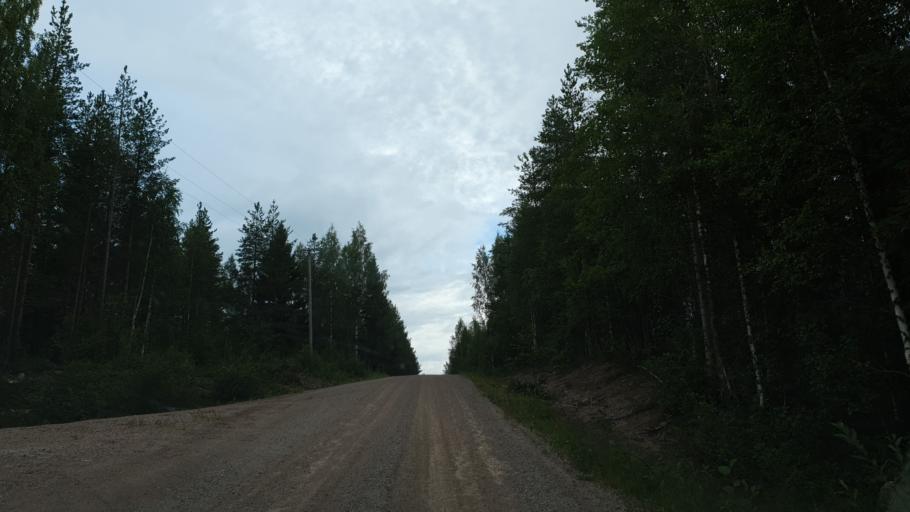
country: FI
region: Kainuu
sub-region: Kehys-Kainuu
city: Suomussalmi
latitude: 64.4528
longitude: 28.9754
